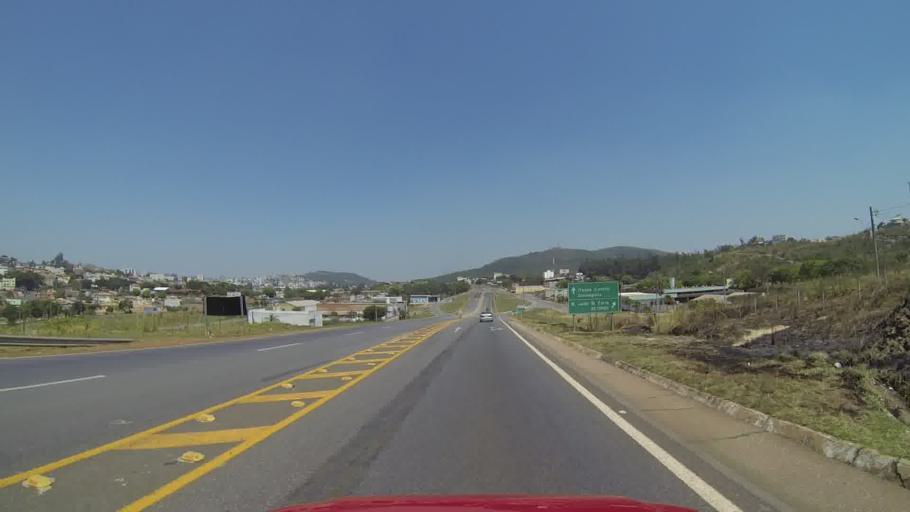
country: BR
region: Minas Gerais
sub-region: Itauna
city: Itauna
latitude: -20.0626
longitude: -44.5575
